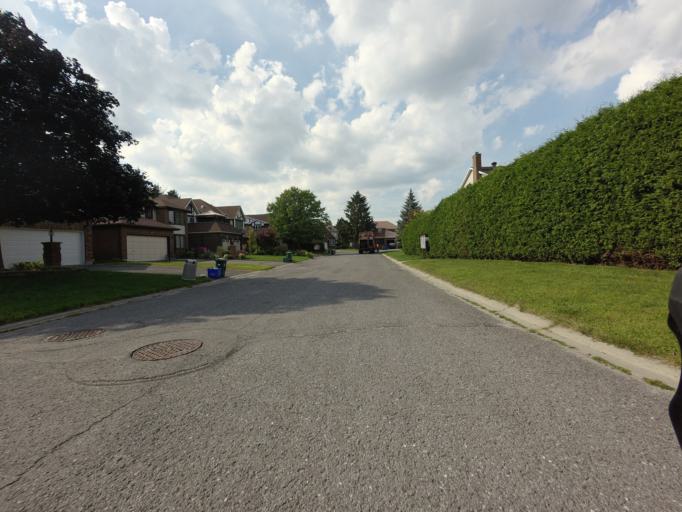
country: CA
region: Ontario
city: Bells Corners
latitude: 45.3275
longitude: -75.7729
